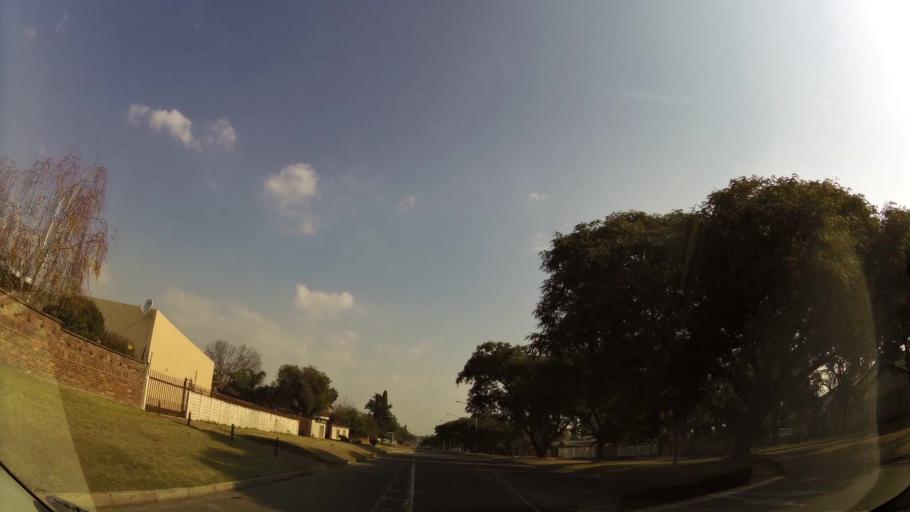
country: ZA
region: Gauteng
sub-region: Ekurhuleni Metropolitan Municipality
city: Benoni
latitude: -26.1533
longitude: 28.2943
